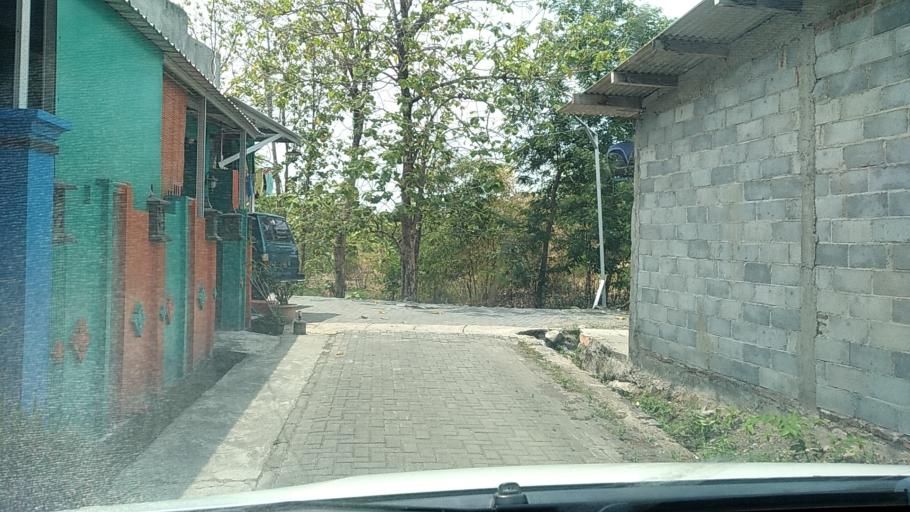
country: ID
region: Central Java
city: Mranggen
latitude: -7.0577
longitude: 110.4796
